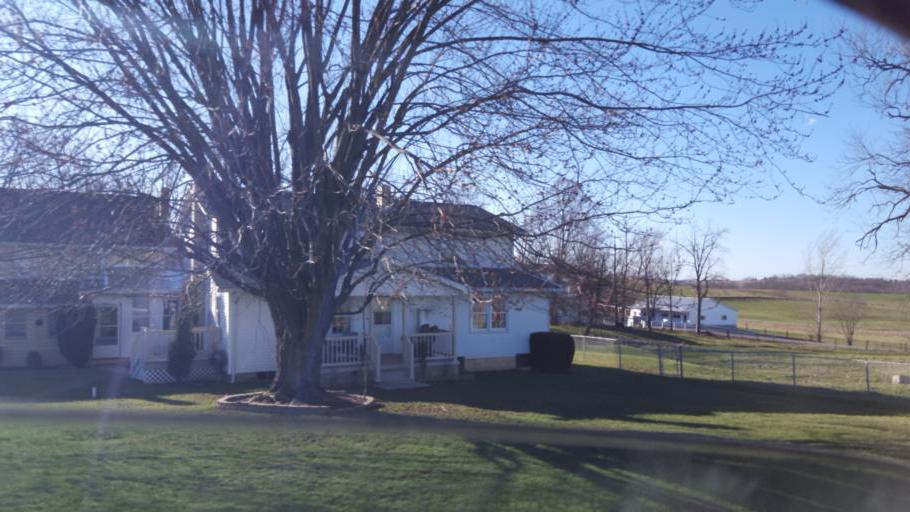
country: US
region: Ohio
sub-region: Tuscarawas County
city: Sugarcreek
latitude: 40.5928
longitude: -81.7613
